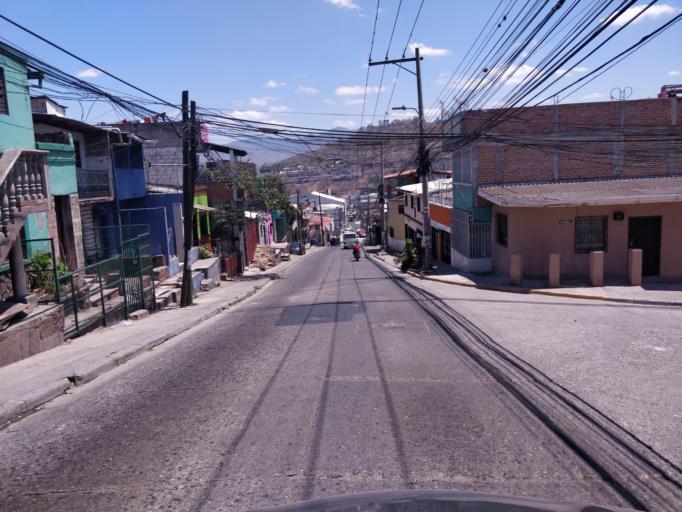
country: HN
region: Francisco Morazan
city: Tegucigalpa
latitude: 14.0957
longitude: -87.2128
